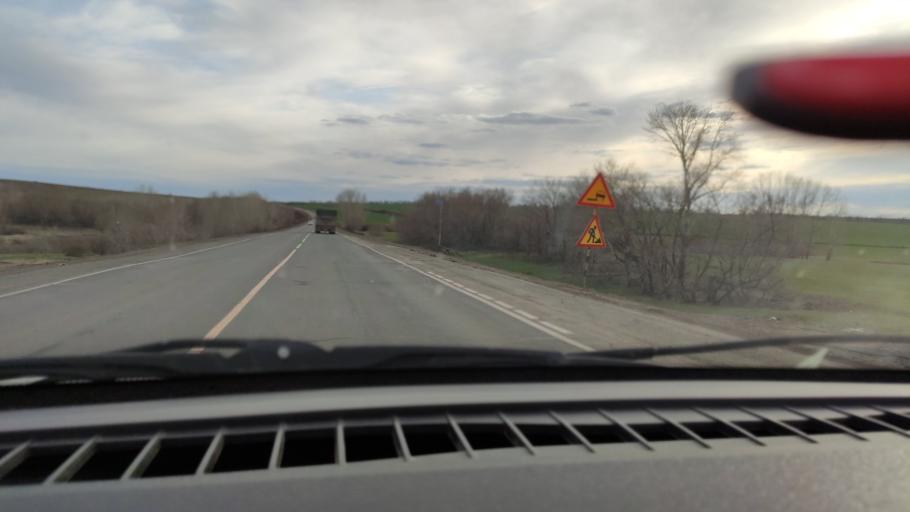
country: RU
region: Orenburg
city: Sakmara
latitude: 52.1914
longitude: 55.3017
